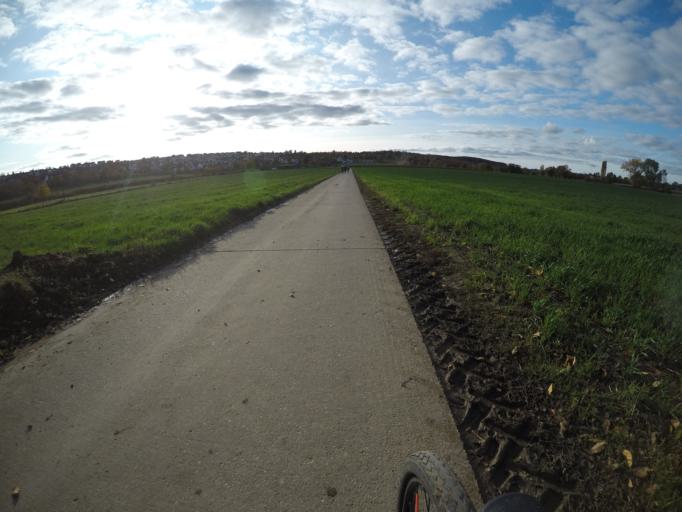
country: DE
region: Baden-Wuerttemberg
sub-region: Regierungsbezirk Stuttgart
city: Leinfelden-Echterdingen
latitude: 48.6749
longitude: 9.1783
